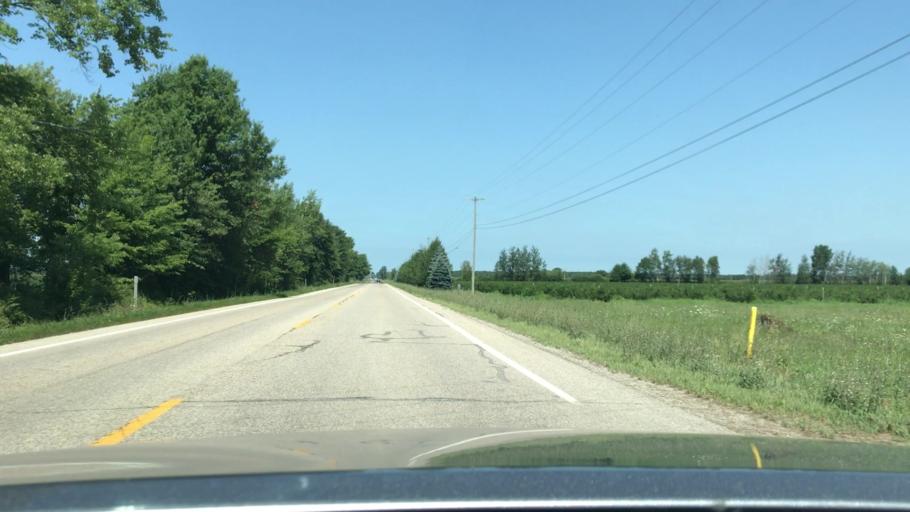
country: US
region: Michigan
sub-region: Ottawa County
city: Allendale
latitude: 42.9575
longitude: -86.0824
